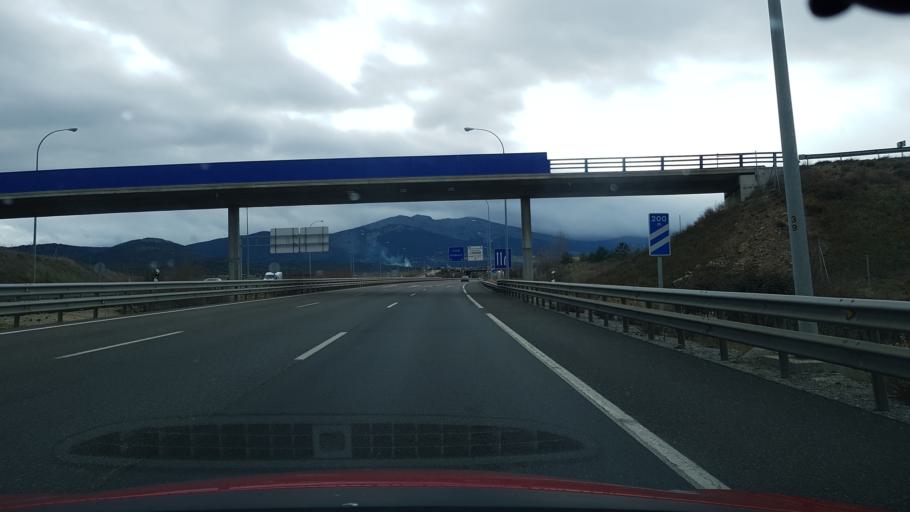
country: ES
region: Castille and Leon
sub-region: Provincia de Segovia
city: Segovia
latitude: 40.9098
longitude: -4.1032
